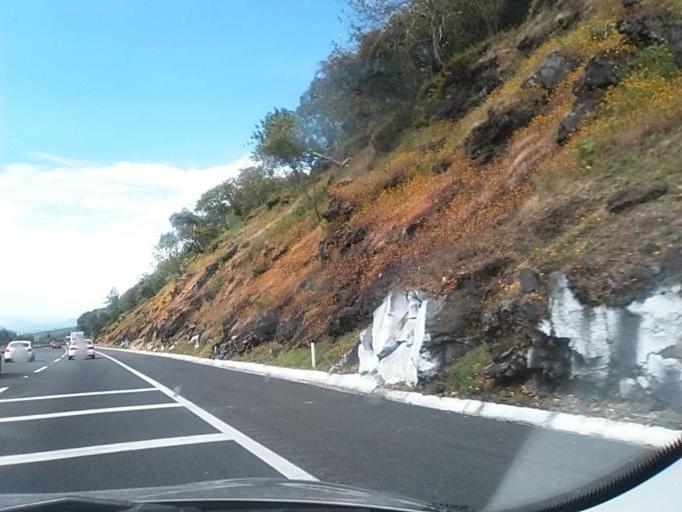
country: MX
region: Morelos
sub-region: Cuernavaca
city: Villa Santiago
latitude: 19.0088
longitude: -99.1751
